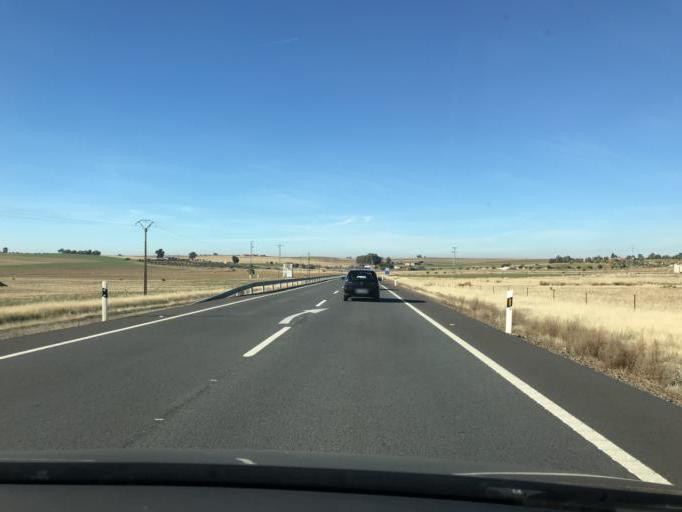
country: ES
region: Extremadura
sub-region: Provincia de Badajoz
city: Granja de Torrehermosa
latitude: 38.3016
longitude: -5.6062
